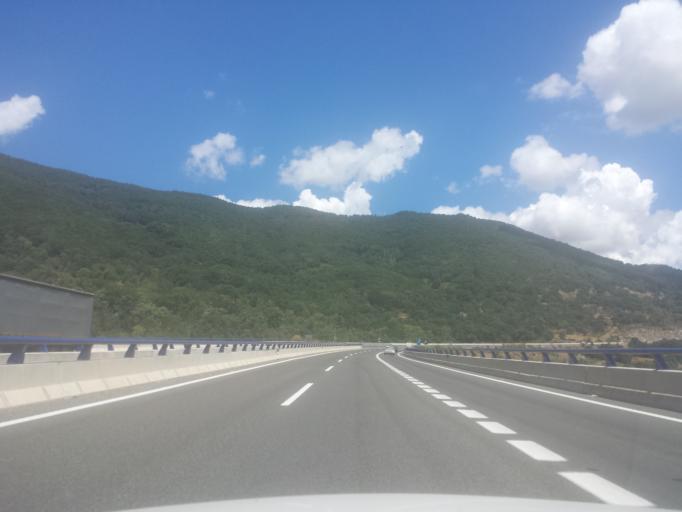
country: ES
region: Extremadura
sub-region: Provincia de Caceres
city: Banos de Montemayor
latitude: 40.3102
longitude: -5.8799
